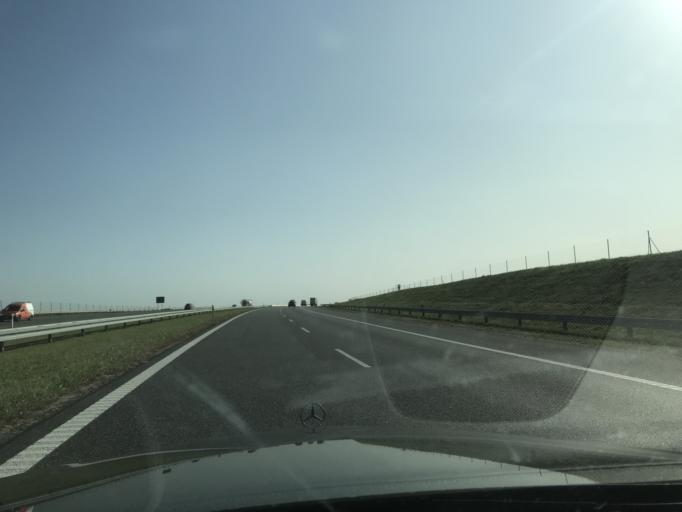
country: PL
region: Subcarpathian Voivodeship
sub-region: Powiat debicki
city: Czarna
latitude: 50.1012
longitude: 21.2330
